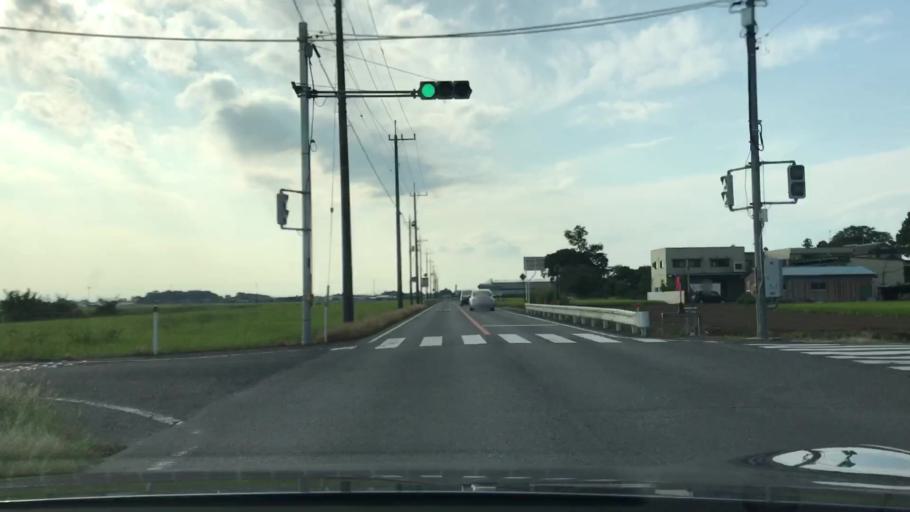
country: JP
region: Saitama
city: Gyoda
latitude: 36.2099
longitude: 139.4601
